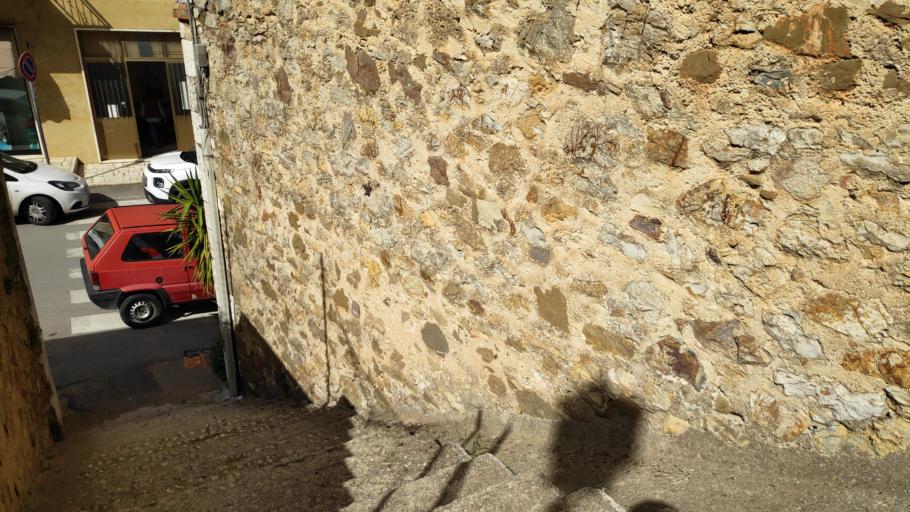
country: IT
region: Tuscany
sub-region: Provincia di Grosseto
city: Manciano
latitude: 42.6210
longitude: 11.4903
